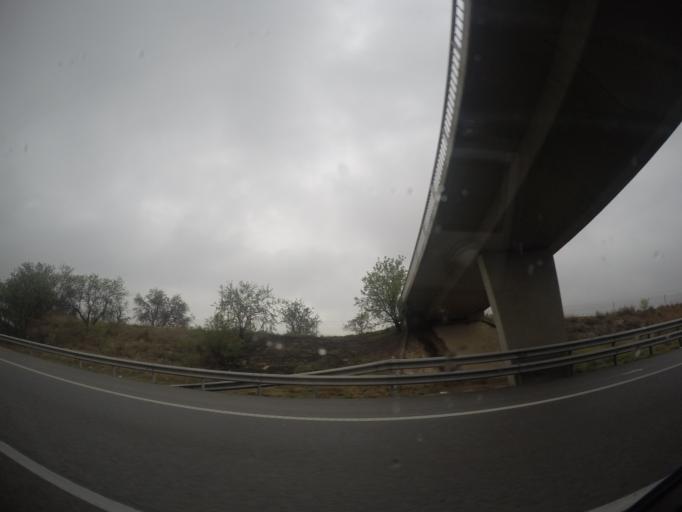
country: ES
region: Catalonia
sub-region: Provincia de Barcelona
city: Vilafranca del Penedes
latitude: 41.3297
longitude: 1.6969
